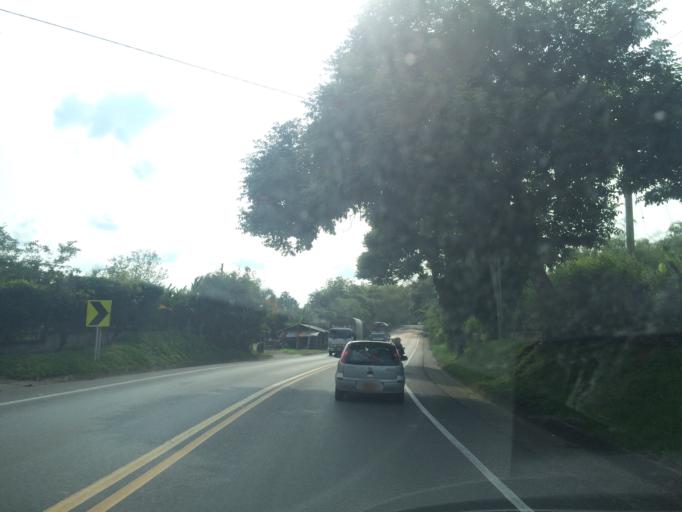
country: CO
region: Quindio
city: La Tebaida
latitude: 4.4495
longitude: -75.8053
